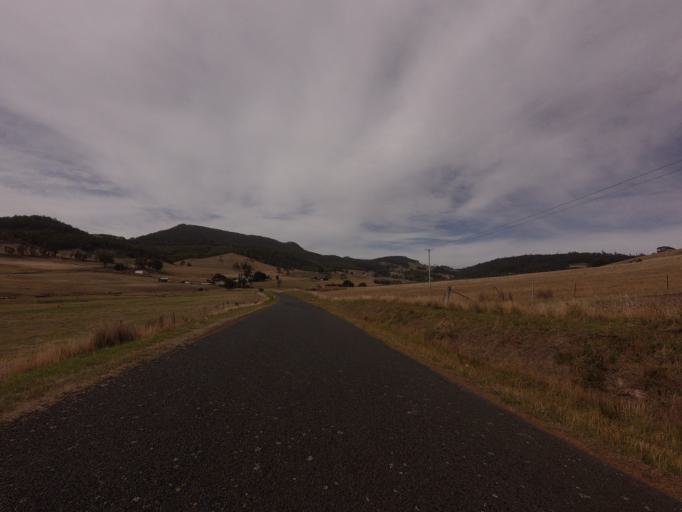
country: AU
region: Tasmania
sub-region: Sorell
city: Sorell
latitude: -42.4772
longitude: 147.5742
